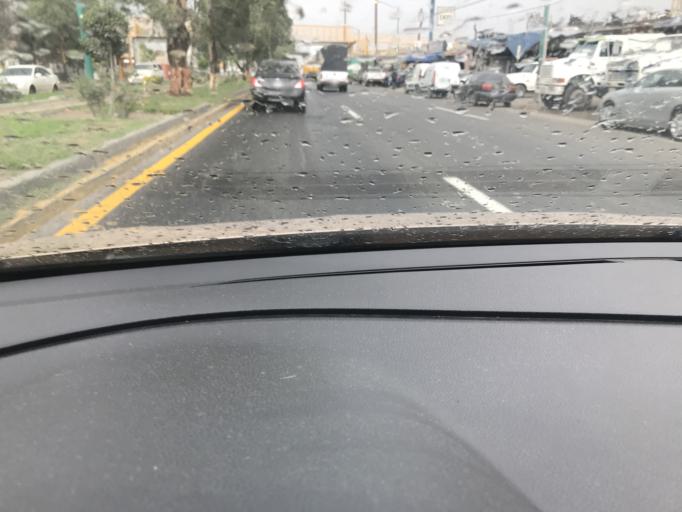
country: MX
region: Mexico
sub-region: La Paz
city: Arenal
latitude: 19.3892
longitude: -98.9360
